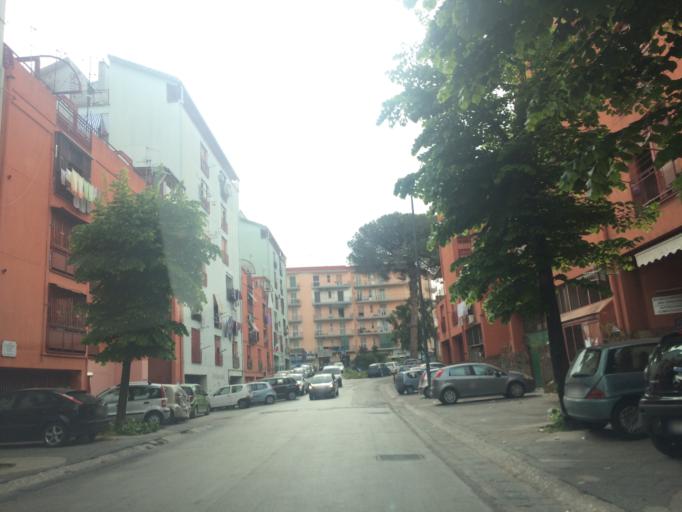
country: IT
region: Campania
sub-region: Provincia di Napoli
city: Mugnano di Napoli
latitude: 40.8913
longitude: 14.2298
